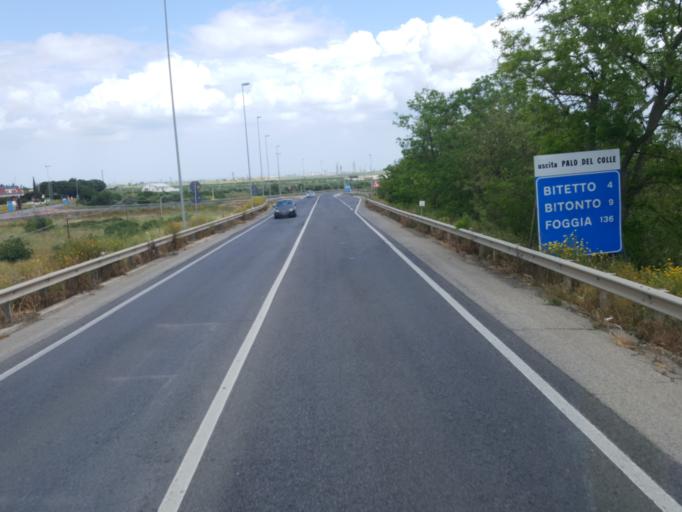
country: IT
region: Apulia
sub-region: Provincia di Bari
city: Palo del Colle
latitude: 41.0546
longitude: 16.7112
